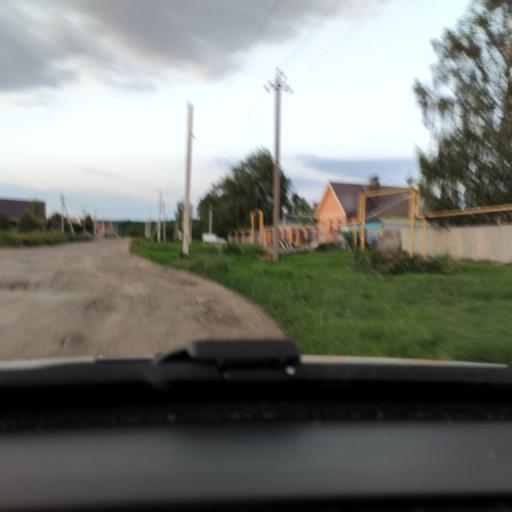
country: RU
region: Voronezj
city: Semiluki
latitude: 51.7474
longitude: 39.0219
